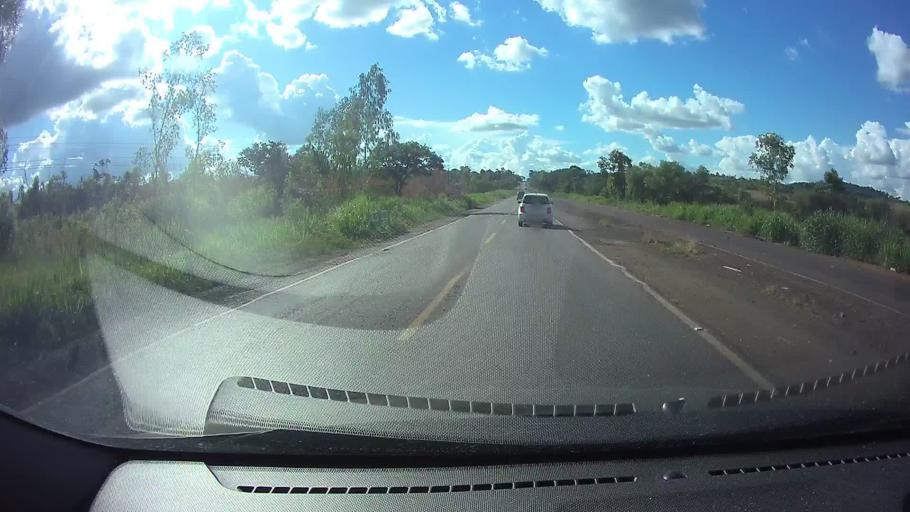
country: PY
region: Cordillera
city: Eusebio Ayala
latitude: -25.4259
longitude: -56.9197
